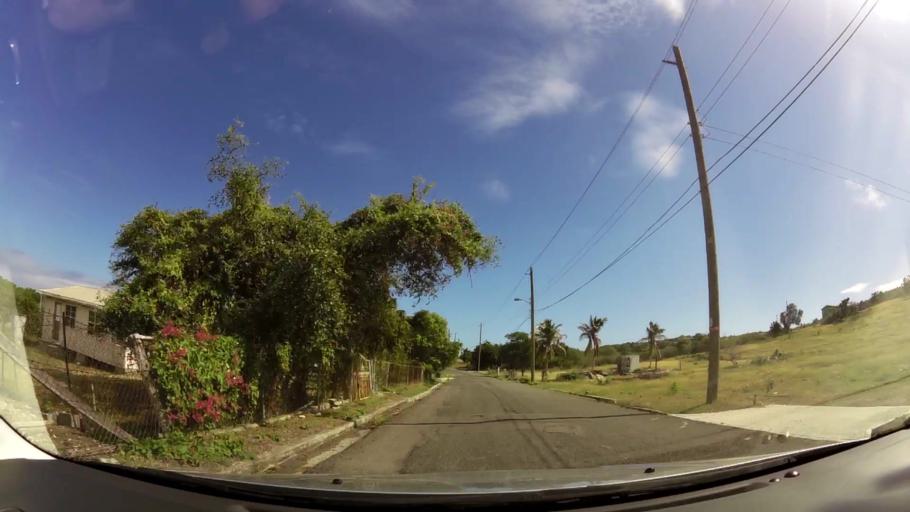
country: AG
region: Saint Paul
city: Falmouth
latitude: 17.0344
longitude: -61.7495
